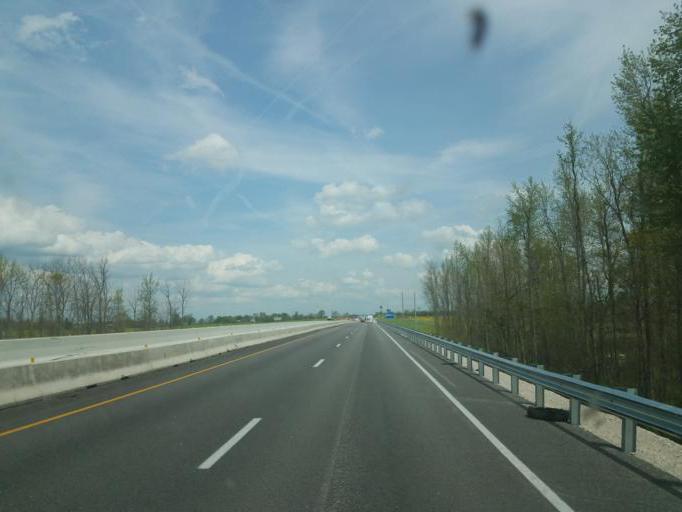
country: US
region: Kentucky
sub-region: Larue County
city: Hodgenville
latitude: 37.5095
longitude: -85.8873
